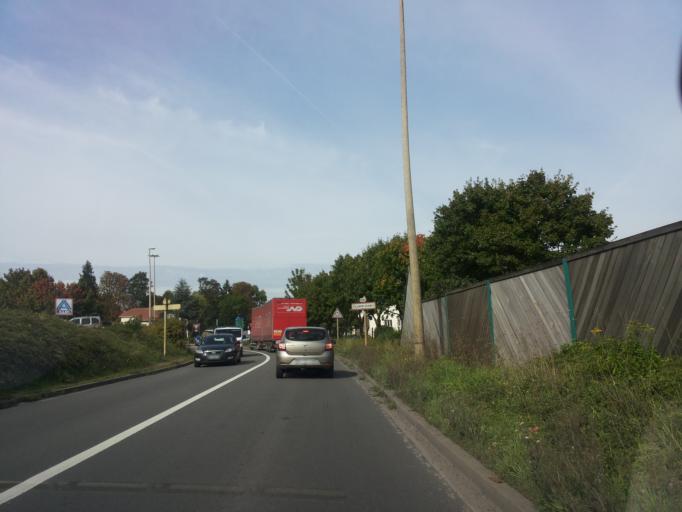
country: FR
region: Nord-Pas-de-Calais
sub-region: Departement du Pas-de-Calais
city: Saint-Laurent-Blangy
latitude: 50.2924
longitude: 2.7953
